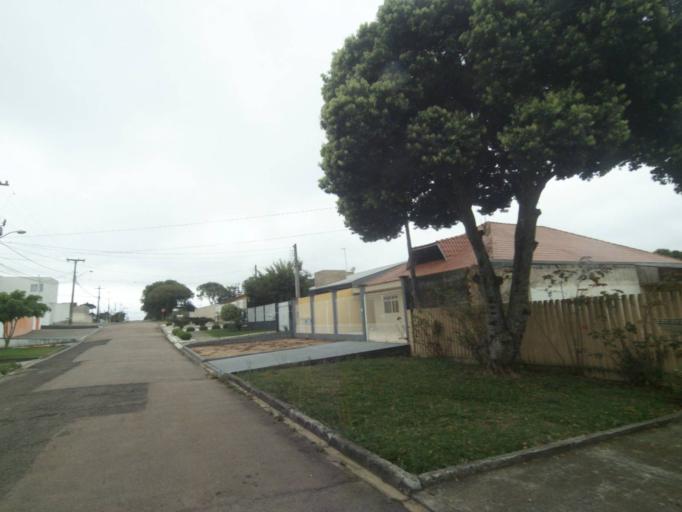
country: BR
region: Parana
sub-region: Sao Jose Dos Pinhais
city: Sao Jose dos Pinhais
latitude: -25.5469
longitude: -49.2844
